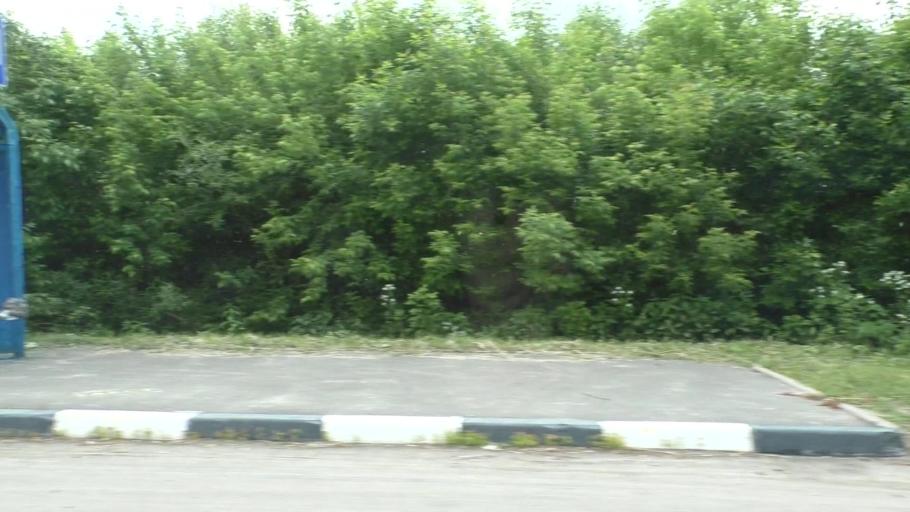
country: RU
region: Moskovskaya
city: Yegor'yevsk
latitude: 55.3963
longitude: 39.0153
